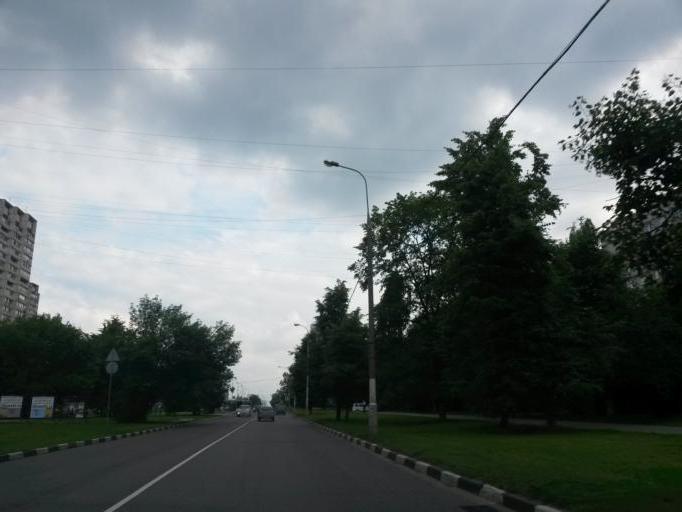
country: RU
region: Moscow
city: Orekhovo-Borisovo
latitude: 55.6254
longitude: 37.7424
